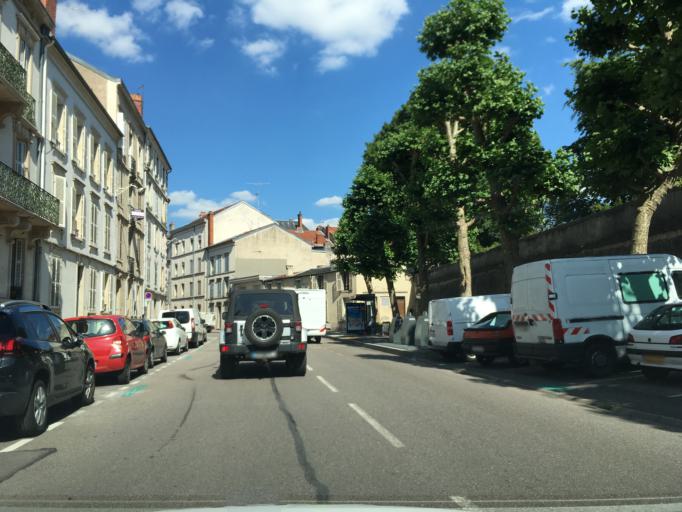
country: FR
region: Lorraine
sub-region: Departement de Meurthe-et-Moselle
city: Maxeville
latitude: 48.7004
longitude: 6.1783
